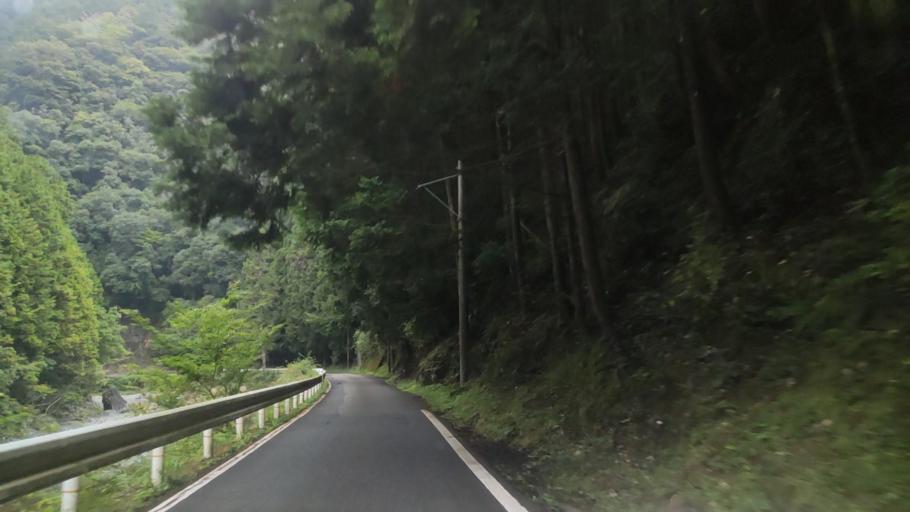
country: JP
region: Wakayama
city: Hashimoto
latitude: 34.2665
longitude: 135.6445
